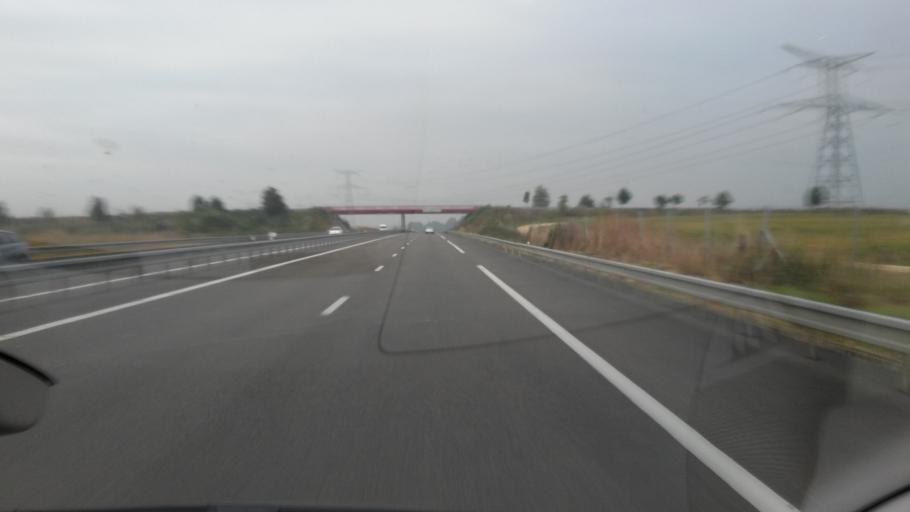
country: FR
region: Champagne-Ardenne
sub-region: Departement des Ardennes
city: Rethel
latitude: 49.5684
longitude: 4.4719
